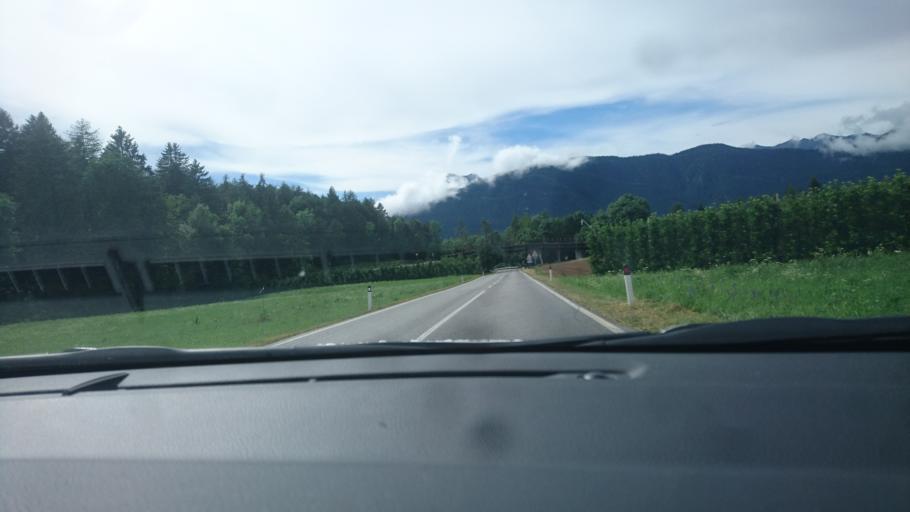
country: IT
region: Trentino-Alto Adige
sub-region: Provincia di Trento
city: Romeno
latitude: 46.3896
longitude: 11.1073
